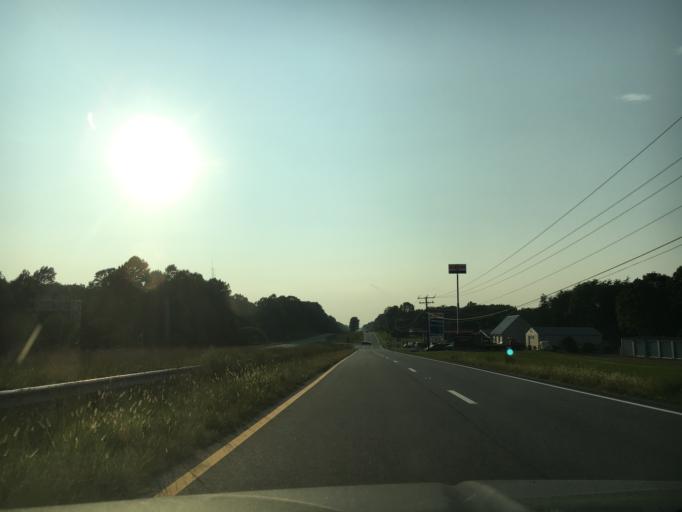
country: US
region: Virginia
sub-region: Appomattox County
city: Appomattox
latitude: 37.2781
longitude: -78.6939
